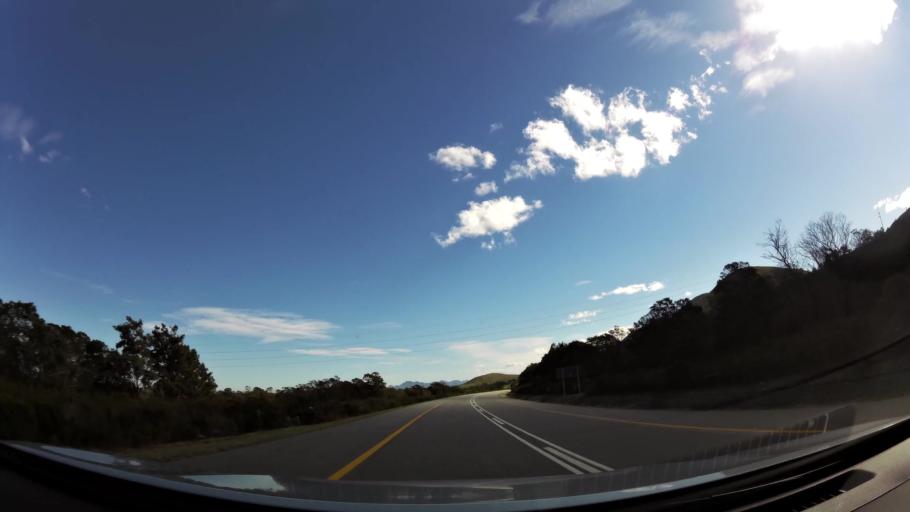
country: ZA
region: Eastern Cape
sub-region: Cacadu District Municipality
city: Kruisfontein
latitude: -33.9957
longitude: 24.7106
